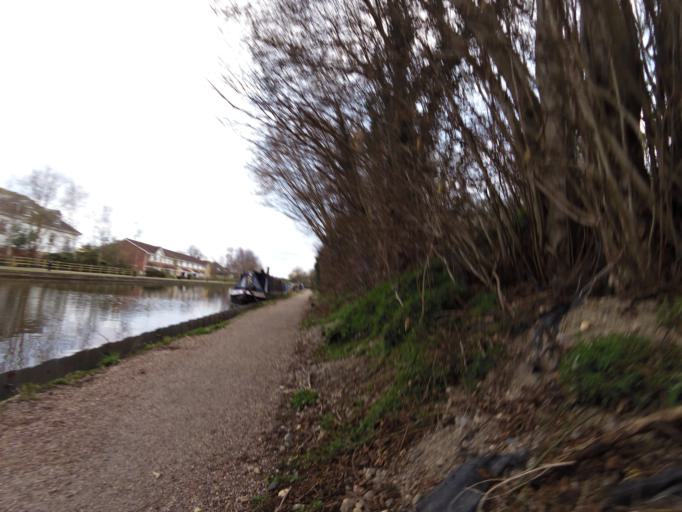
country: GB
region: England
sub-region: Hertfordshire
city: Rickmansworth
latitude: 51.6465
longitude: -0.4369
